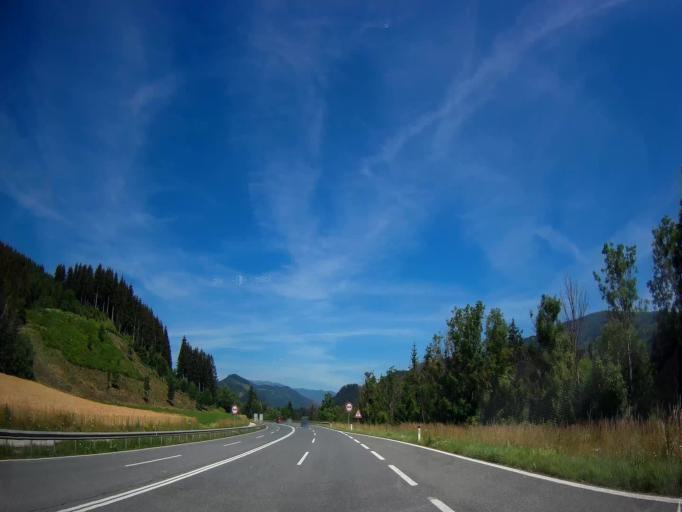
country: AT
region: Carinthia
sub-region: Politischer Bezirk Sankt Veit an der Glan
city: Althofen
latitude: 46.8781
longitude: 14.4508
